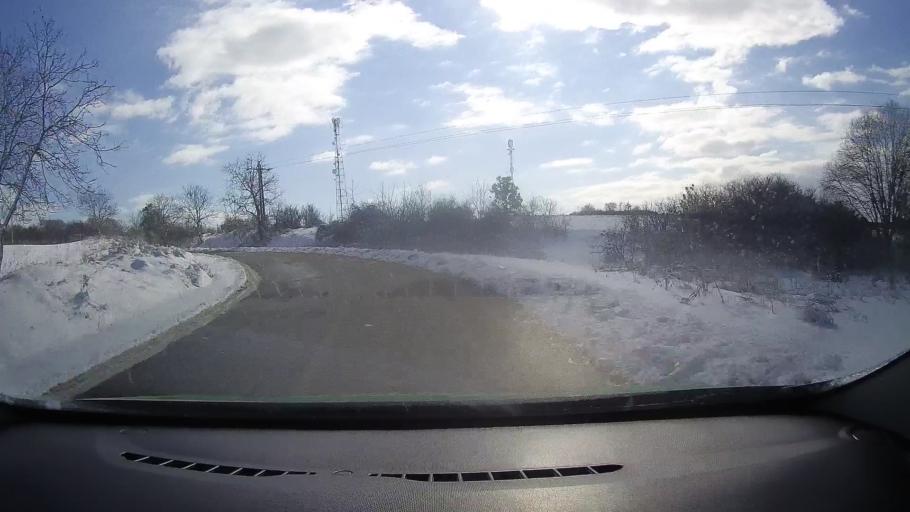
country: RO
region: Sibiu
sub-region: Comuna Mihaileni
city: Mihaileni
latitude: 46.0029
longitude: 24.4258
